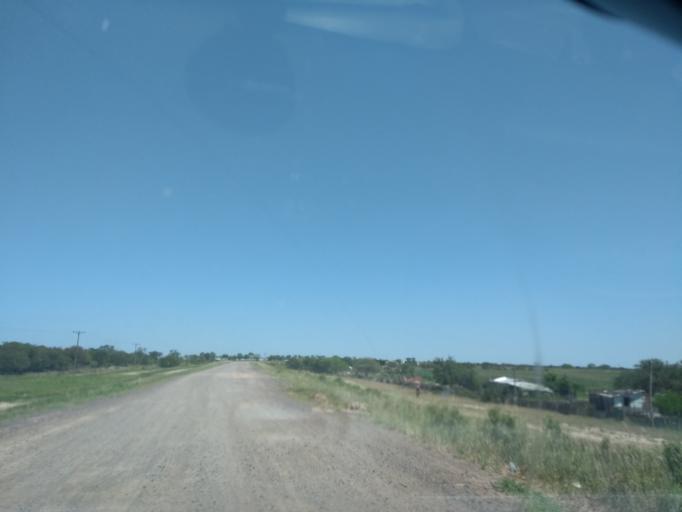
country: AR
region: Chaco
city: Resistencia
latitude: -27.4080
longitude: -58.9538
